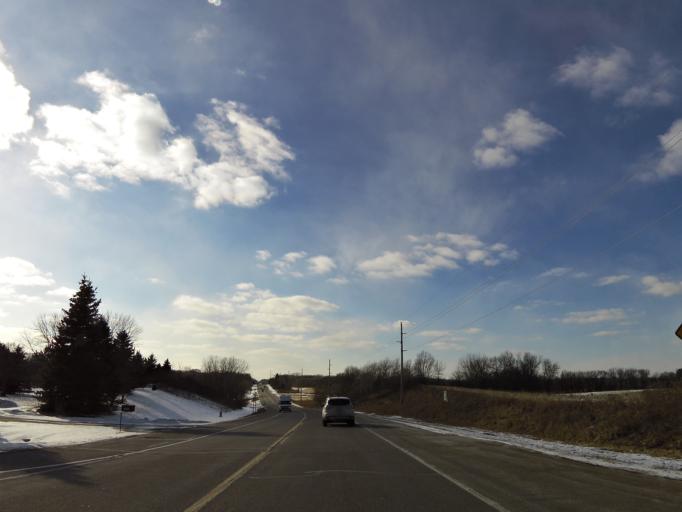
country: US
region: Minnesota
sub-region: Dakota County
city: Rosemount
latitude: 44.7681
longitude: -93.1233
